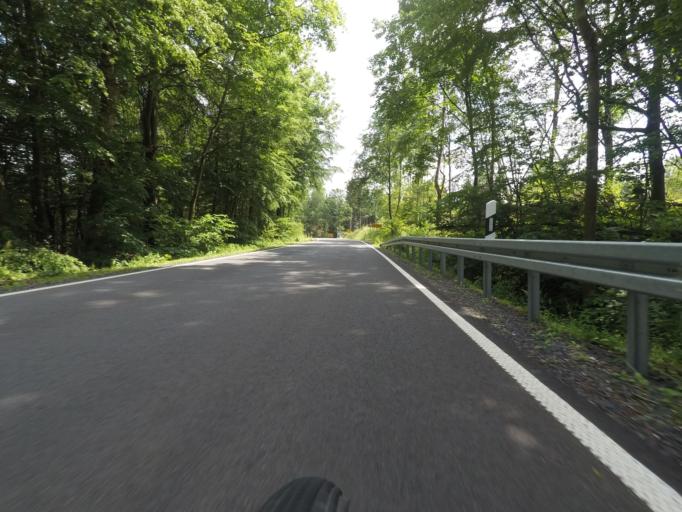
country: DE
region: Hesse
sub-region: Regierungsbezirk Kassel
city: Grossalmerode
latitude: 51.2426
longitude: 9.8768
